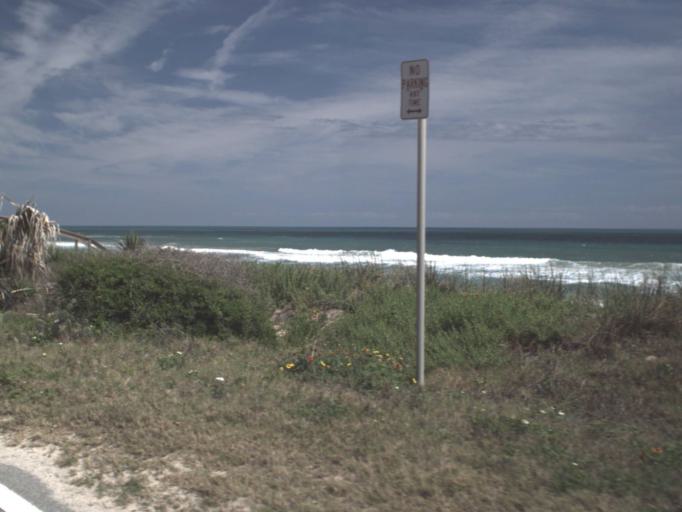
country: US
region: Florida
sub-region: Flagler County
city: Flagler Beach
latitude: 29.4439
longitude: -81.1102
